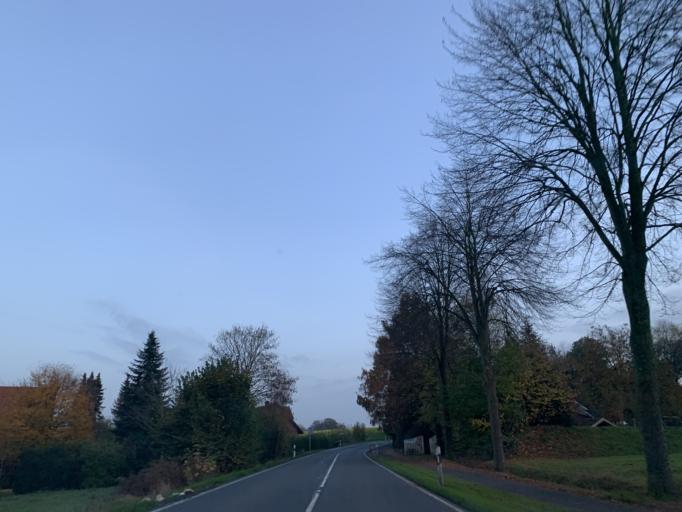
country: DE
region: North Rhine-Westphalia
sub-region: Regierungsbezirk Munster
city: Havixbeck
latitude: 51.9666
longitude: 7.4105
